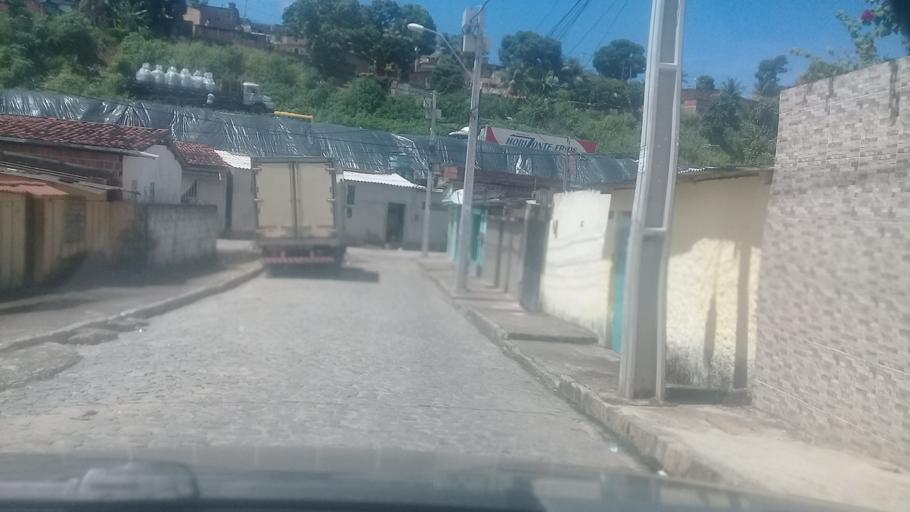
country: BR
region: Pernambuco
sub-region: Jaboatao Dos Guararapes
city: Jaboatao dos Guararapes
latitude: -8.1223
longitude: -34.9441
